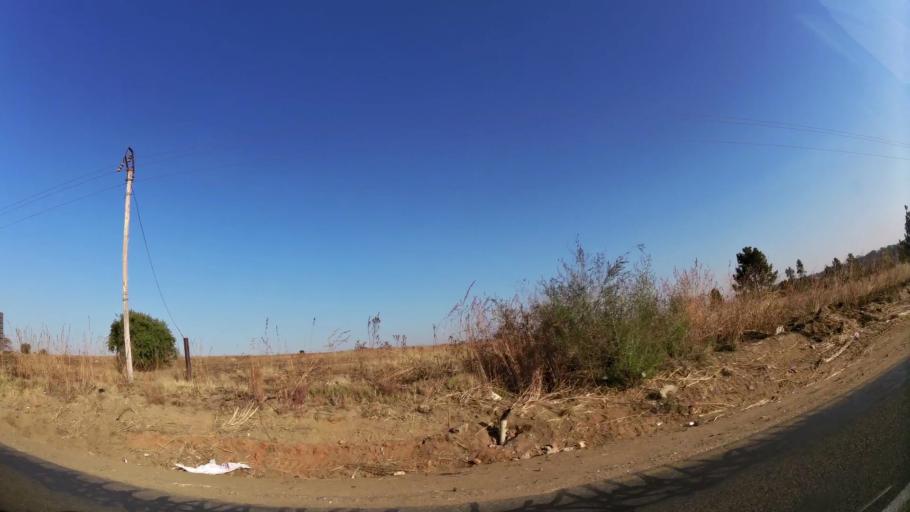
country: ZA
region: Gauteng
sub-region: West Rand District Municipality
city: Muldersdriseloop
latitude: -26.0055
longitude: 27.9113
